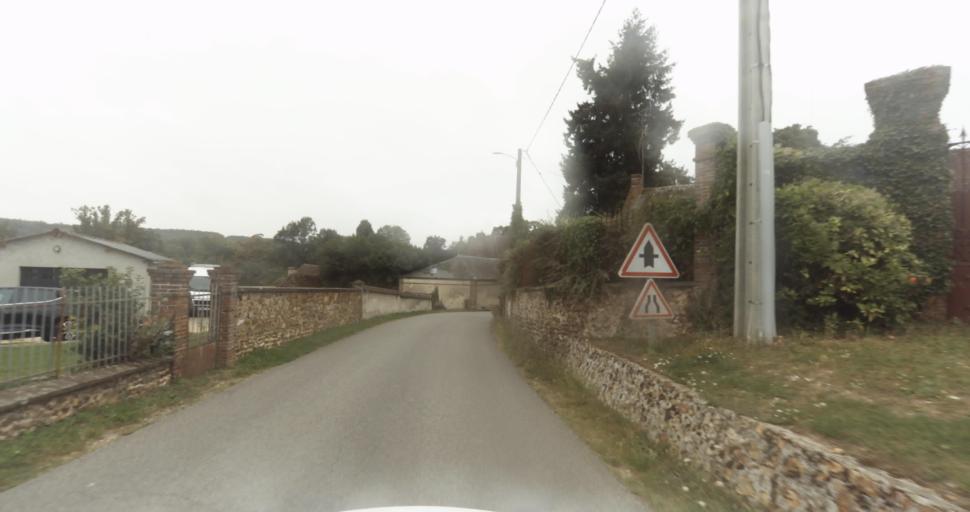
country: FR
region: Haute-Normandie
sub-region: Departement de l'Eure
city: Saint-Germain-sur-Avre
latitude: 48.7646
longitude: 1.2630
